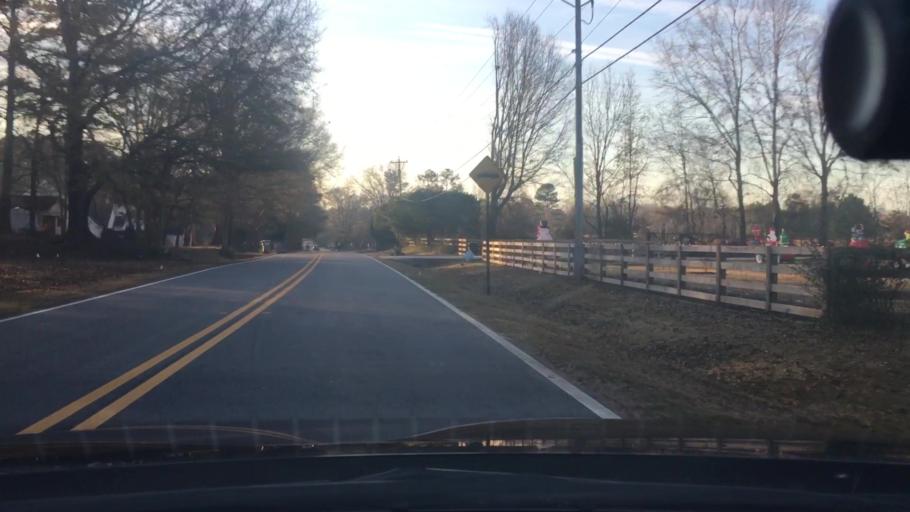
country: US
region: Georgia
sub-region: Coweta County
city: Senoia
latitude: 33.2960
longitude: -84.4608
